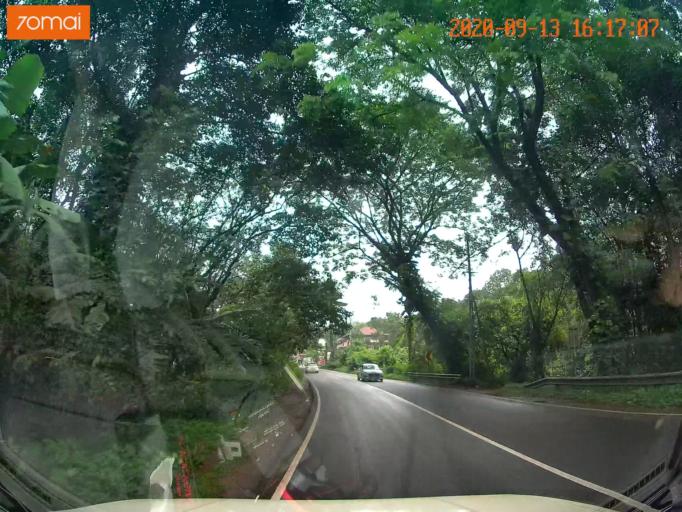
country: IN
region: Kerala
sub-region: Kottayam
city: Lalam
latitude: 9.6994
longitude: 76.6533
